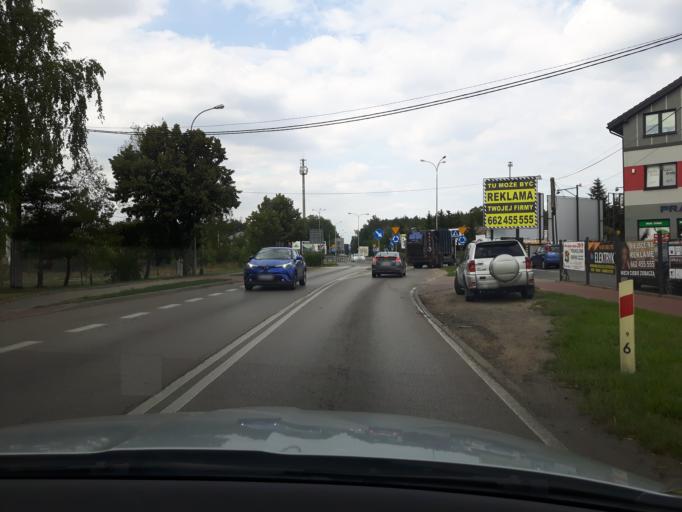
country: PL
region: Masovian Voivodeship
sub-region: Powiat legionowski
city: Stanislawow Pierwszy
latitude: 52.3776
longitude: 21.0292
